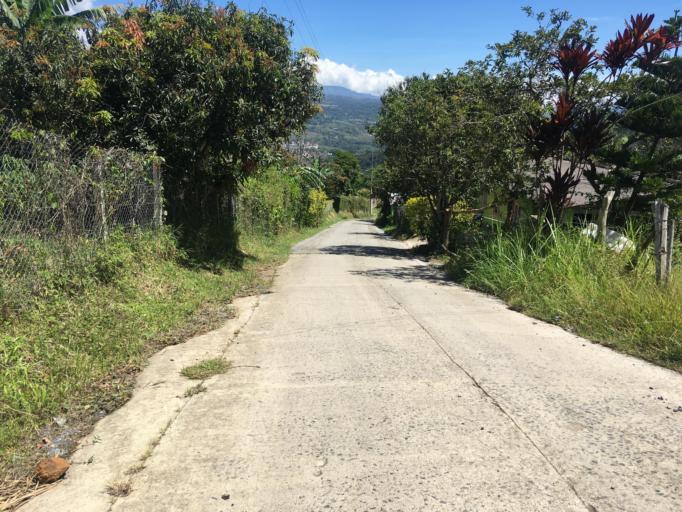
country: CO
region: Santander
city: Barbosa
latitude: 5.9140
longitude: -73.5982
